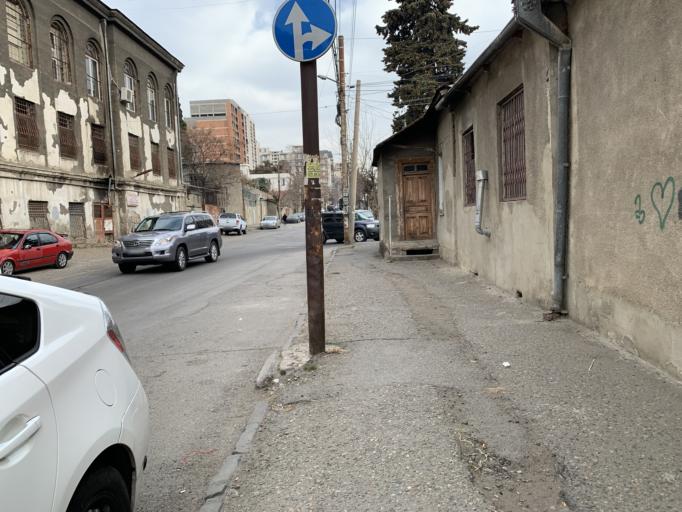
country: GE
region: T'bilisi
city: Tbilisi
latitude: 41.6782
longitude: 44.8396
